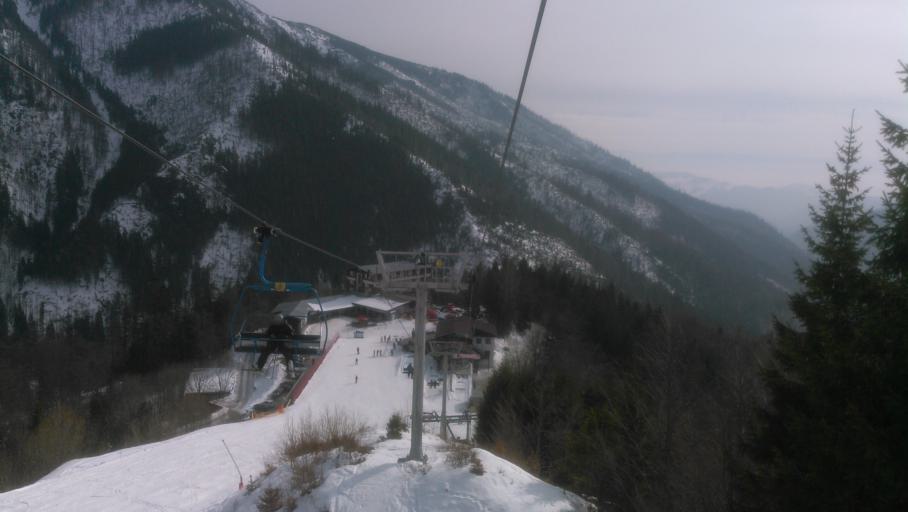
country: SK
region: Banskobystricky
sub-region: Okres Banska Bystrica
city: Brezno
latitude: 48.9260
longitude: 19.6011
